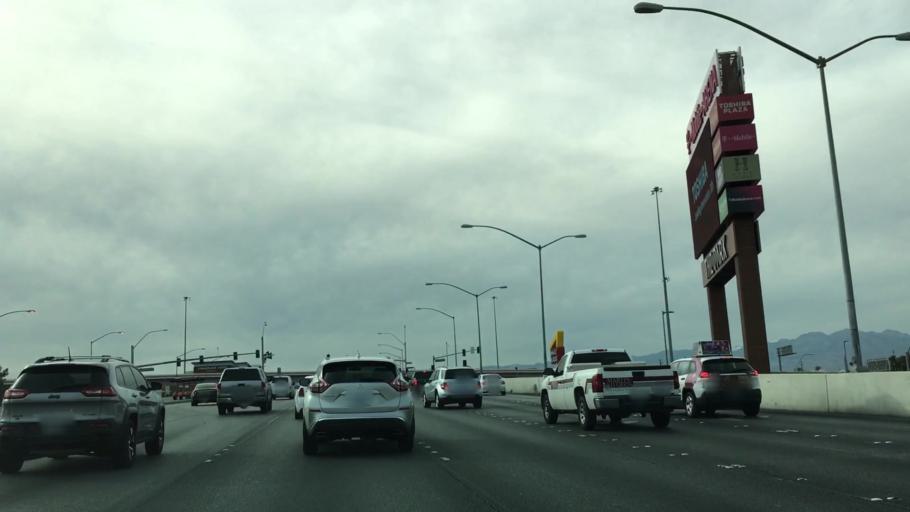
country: US
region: Nevada
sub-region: Clark County
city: Paradise
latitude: 36.1009
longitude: -115.1781
